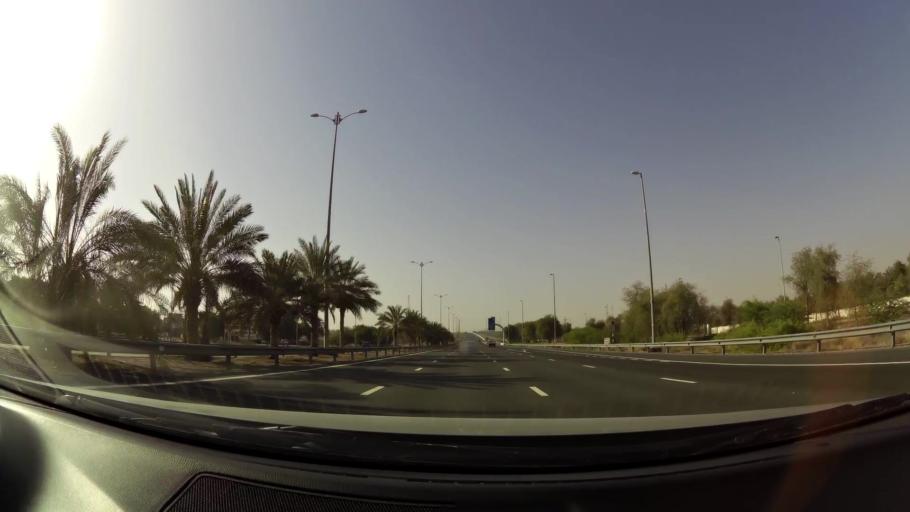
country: OM
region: Al Buraimi
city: Al Buraymi
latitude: 24.5897
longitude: 55.7383
